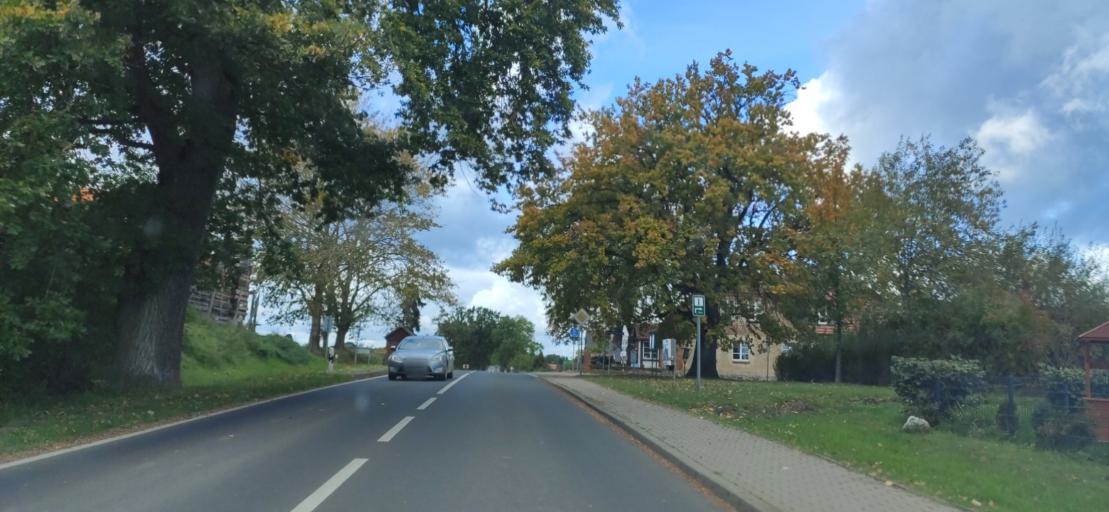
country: DE
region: Mecklenburg-Vorpommern
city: Grabowhofe
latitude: 53.6308
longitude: 12.5703
